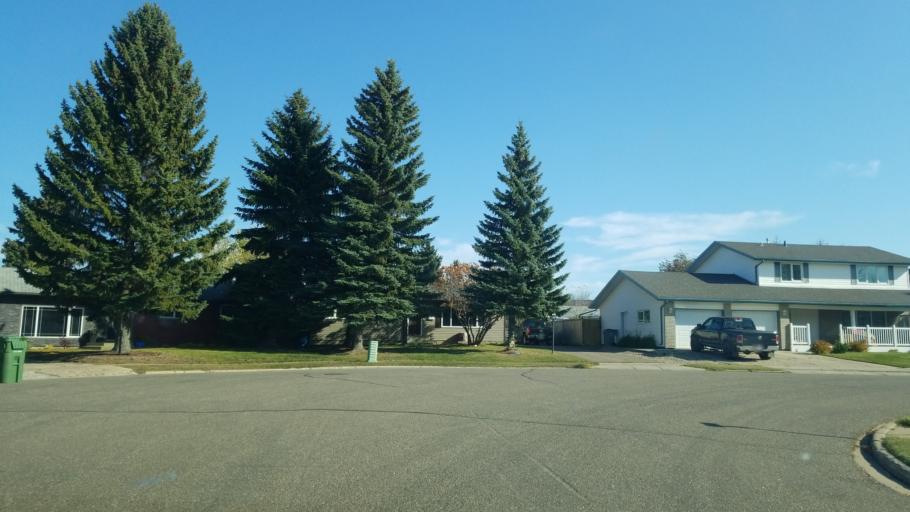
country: CA
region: Saskatchewan
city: Lloydminster
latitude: 53.2692
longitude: -110.0134
